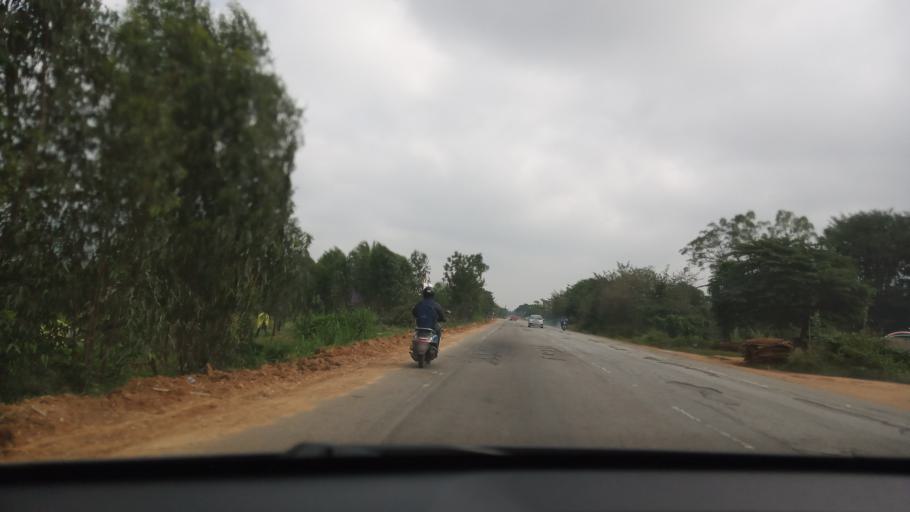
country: IN
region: Karnataka
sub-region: Chikkaballapur
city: Chintamani
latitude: 13.3303
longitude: 77.9969
